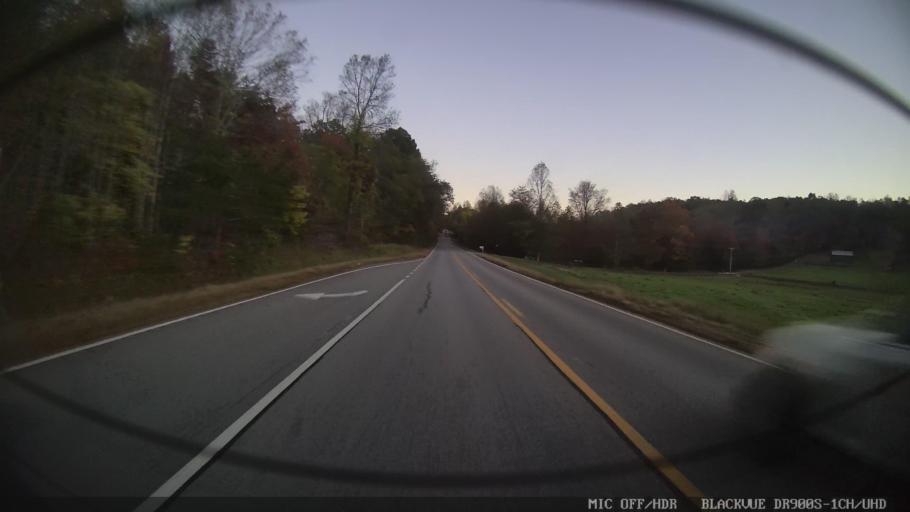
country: US
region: North Carolina
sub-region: Clay County
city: Hayesville
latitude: 34.9639
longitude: -83.8732
